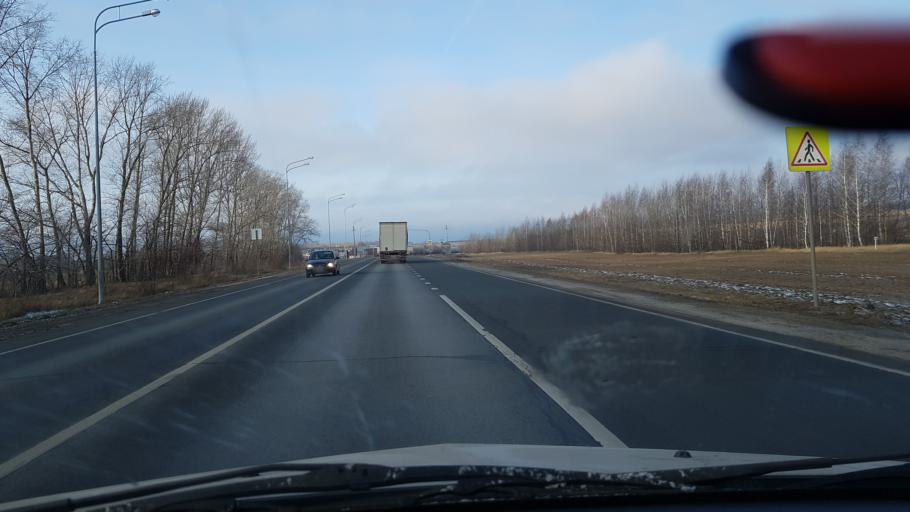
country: RU
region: Tatarstan
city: Laishevo
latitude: 55.3909
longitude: 49.8108
